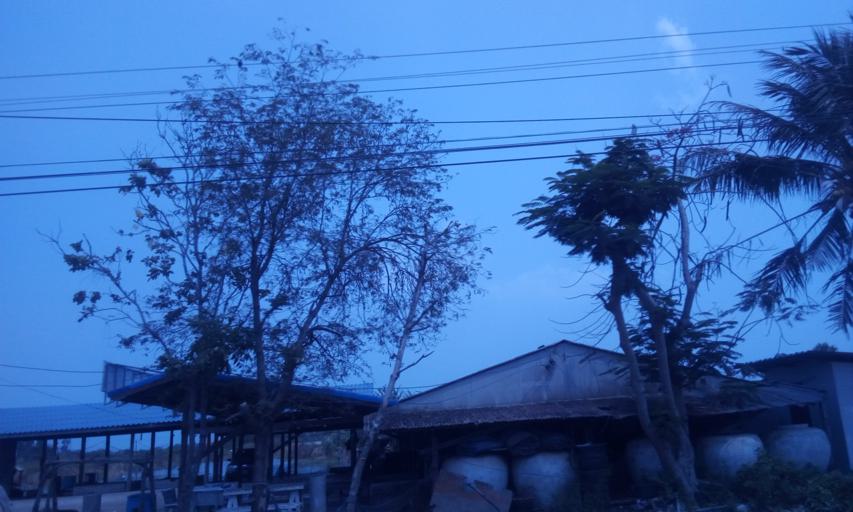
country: TH
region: Chachoengsao
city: Ban Pho
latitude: 13.5946
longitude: 101.1198
